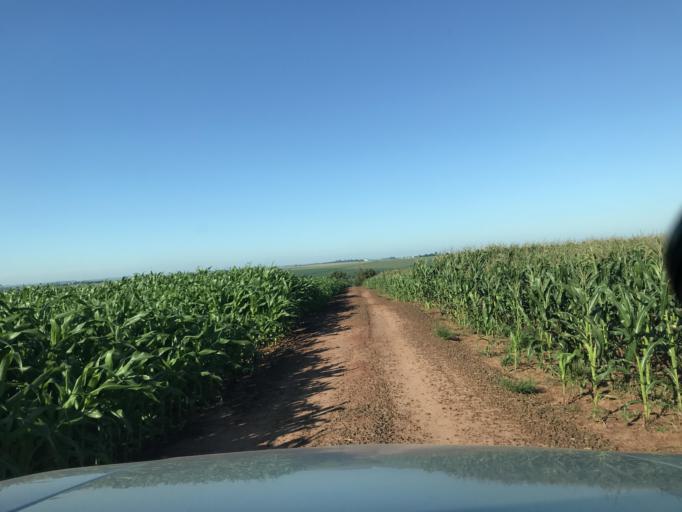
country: BR
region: Parana
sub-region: Palotina
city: Palotina
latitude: -24.2327
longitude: -53.7636
